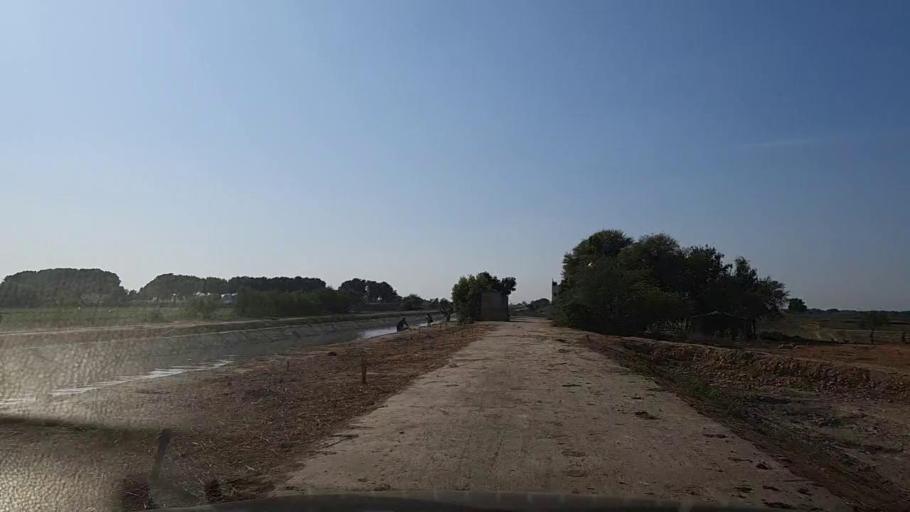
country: PK
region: Sindh
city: Mirpur Sakro
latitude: 24.5973
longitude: 67.8006
